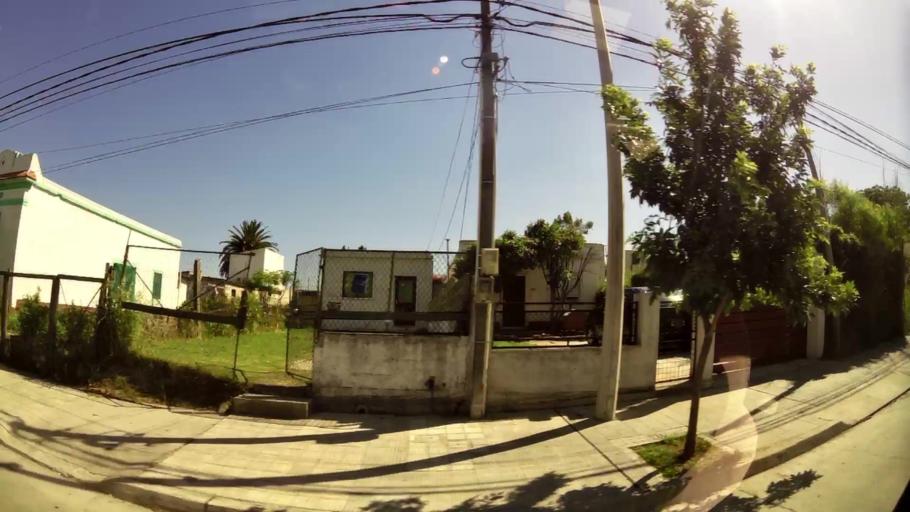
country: UY
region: Canelones
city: La Paz
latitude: -34.8390
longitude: -56.2485
